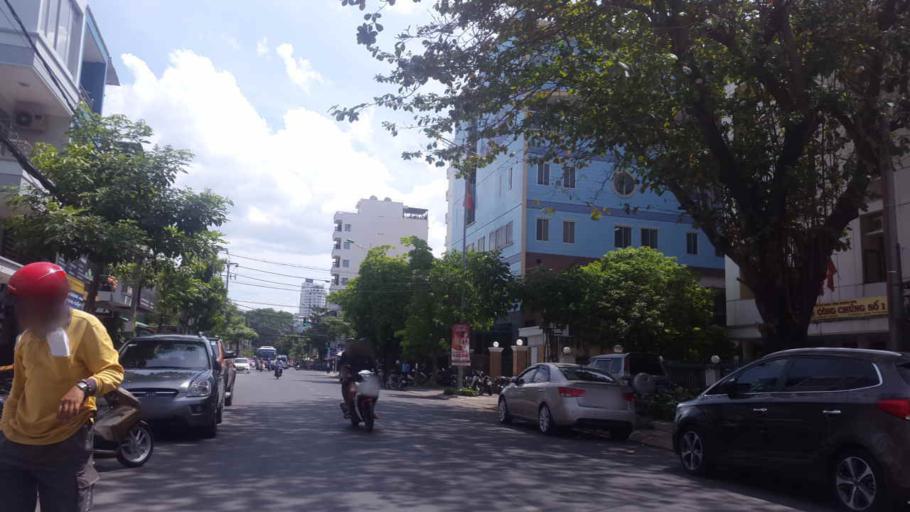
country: VN
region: Khanh Hoa
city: Nha Trang
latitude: 12.2484
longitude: 109.1940
